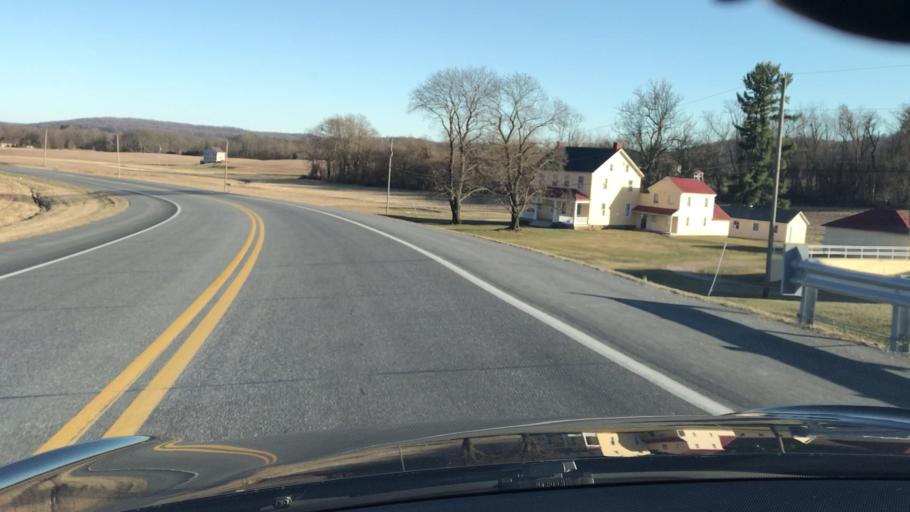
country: US
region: Pennsylvania
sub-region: Cumberland County
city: Lower Allen
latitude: 40.1480
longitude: -76.8829
